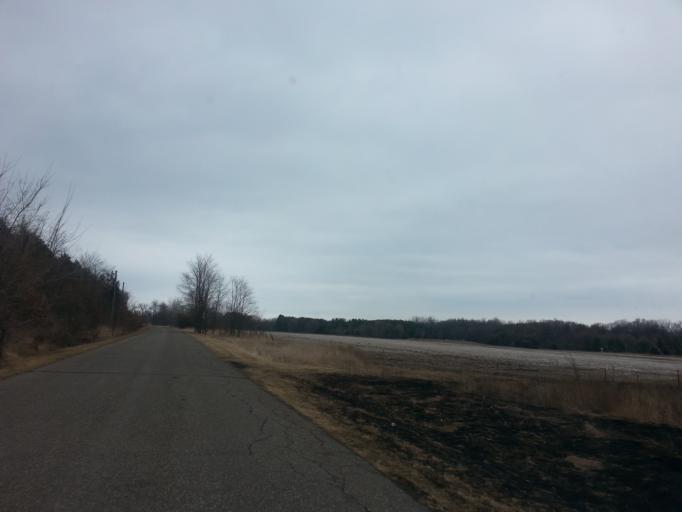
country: US
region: Wisconsin
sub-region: Saint Croix County
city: North Hudson
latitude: 44.9856
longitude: -92.7769
